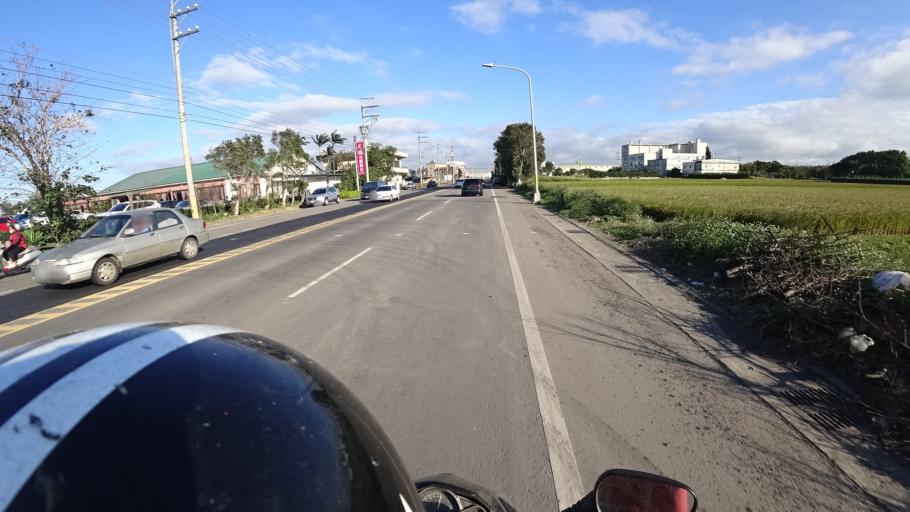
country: TW
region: Taiwan
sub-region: Hsinchu
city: Zhubei
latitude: 24.9821
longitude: 121.0629
